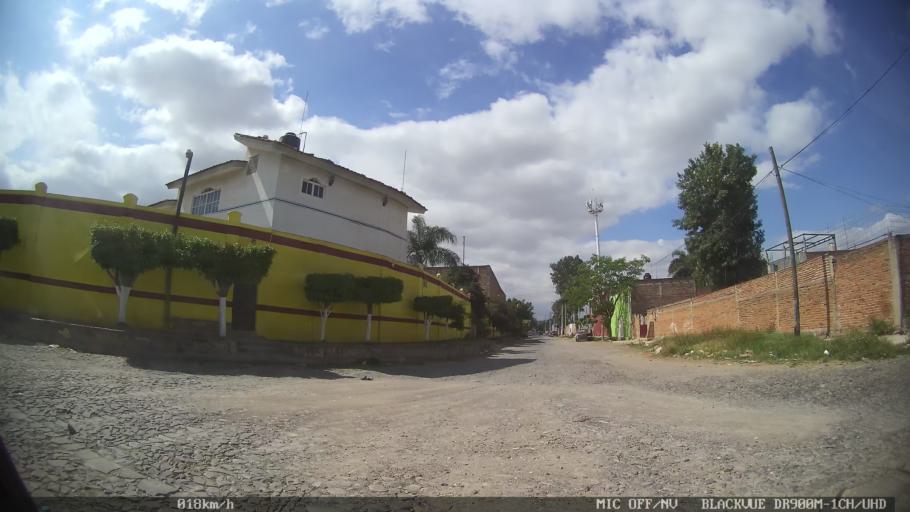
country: MX
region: Jalisco
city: Tonala
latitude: 20.6658
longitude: -103.2425
